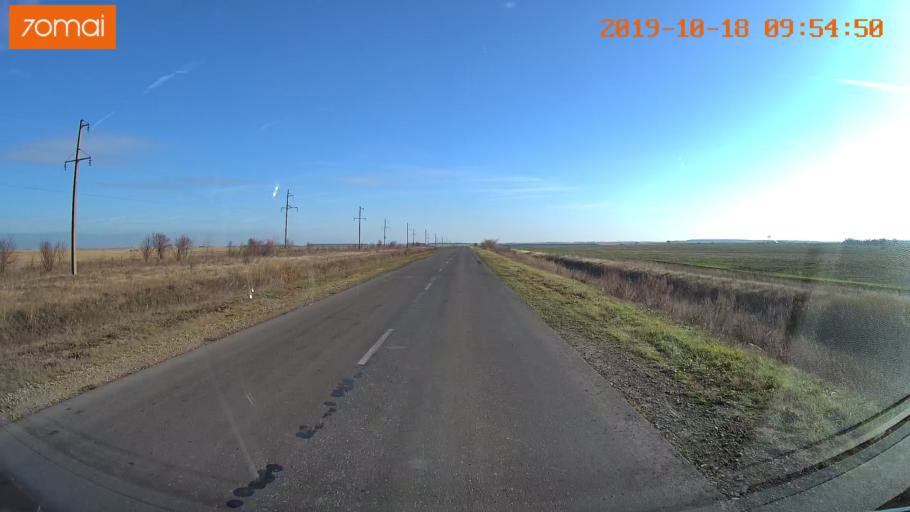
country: RU
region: Tula
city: Kazachka
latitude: 53.3668
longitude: 38.3504
